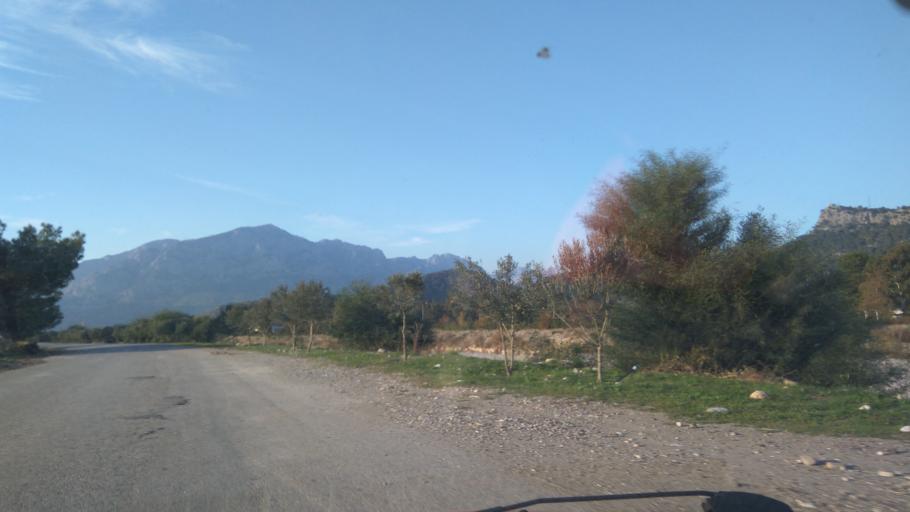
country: TR
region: Antalya
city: Kemer
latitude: 36.5650
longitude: 30.5707
